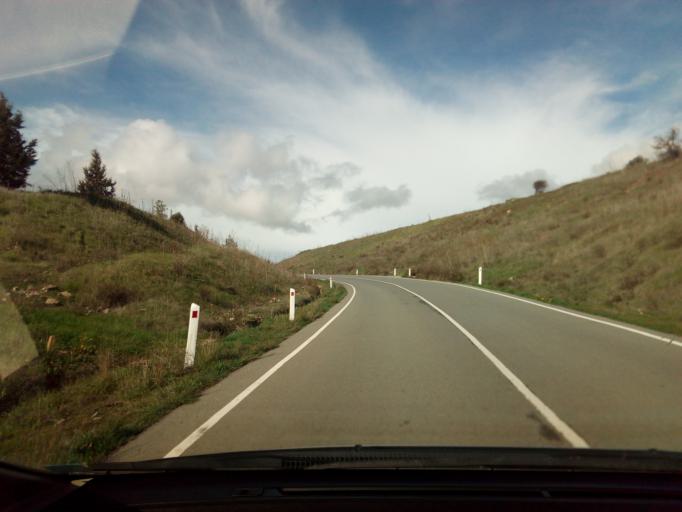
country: CY
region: Pafos
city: Mesogi
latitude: 34.9171
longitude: 32.5402
